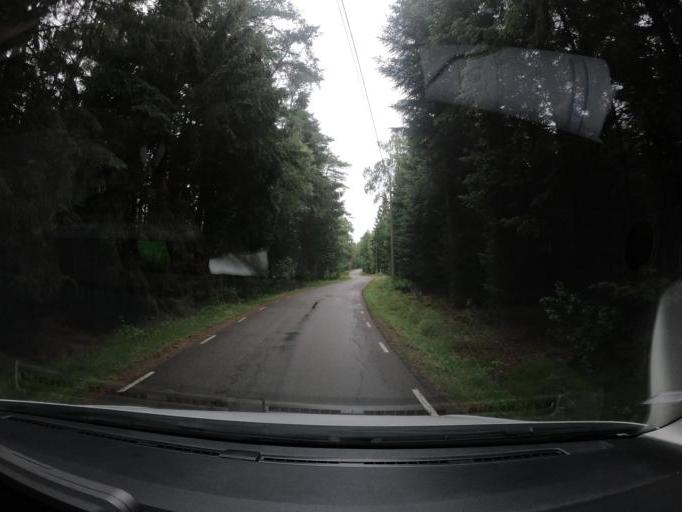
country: SE
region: Skane
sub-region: Orkelljunga Kommun
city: OErkelljunga
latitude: 56.2942
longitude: 13.1198
